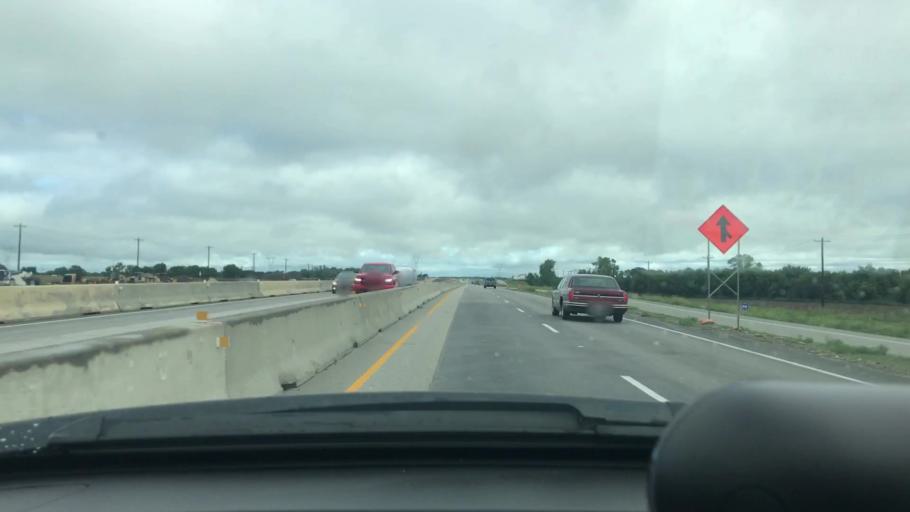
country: US
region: Texas
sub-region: Collin County
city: Anna
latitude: 33.3561
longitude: -96.5844
